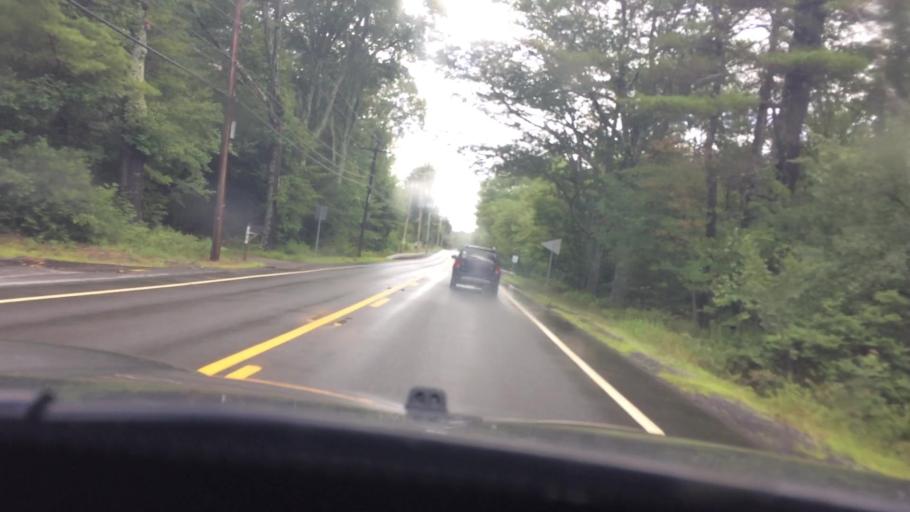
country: US
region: Massachusetts
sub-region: Worcester County
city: Phillipston
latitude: 42.5704
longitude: -72.1394
